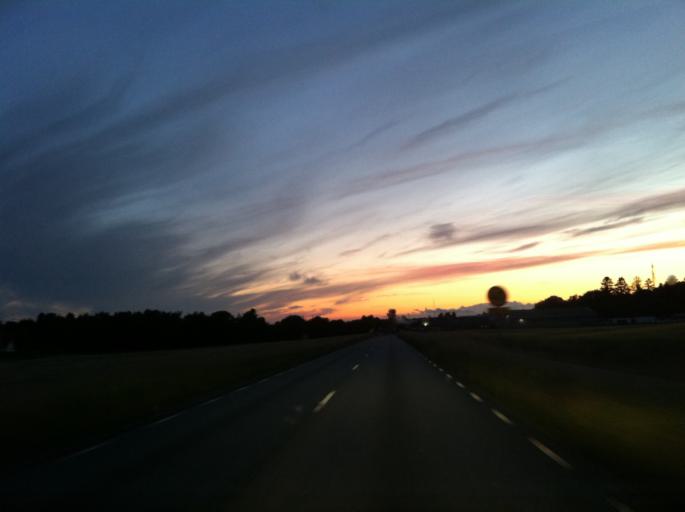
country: SE
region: Skane
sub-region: Sjobo Kommun
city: Sjoebo
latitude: 55.6372
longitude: 13.6824
